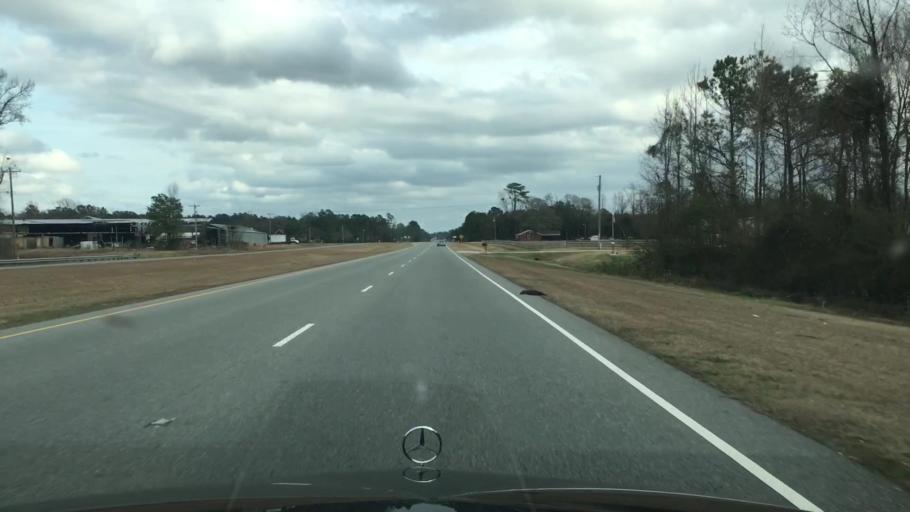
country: US
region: North Carolina
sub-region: Duplin County
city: Beulaville
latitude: 34.9304
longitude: -77.8174
